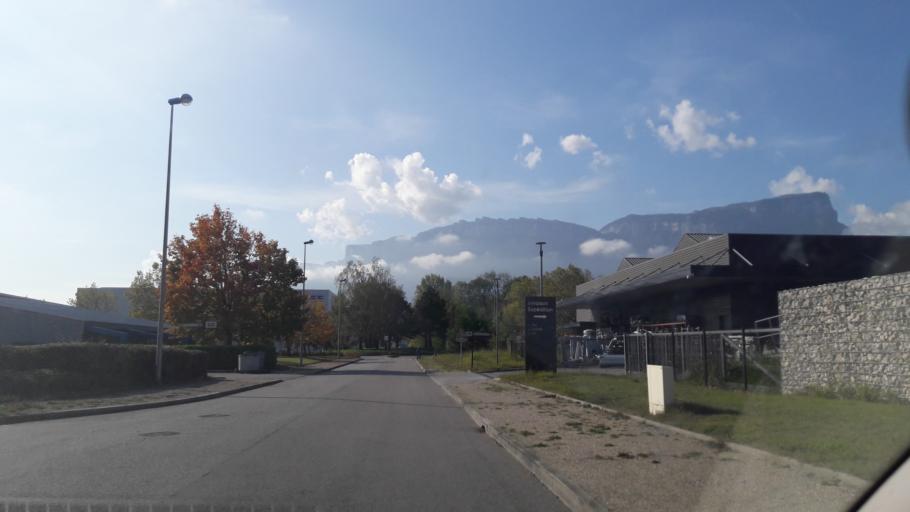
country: FR
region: Rhone-Alpes
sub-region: Departement de la Savoie
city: Montmelian
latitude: 45.4770
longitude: 6.0339
